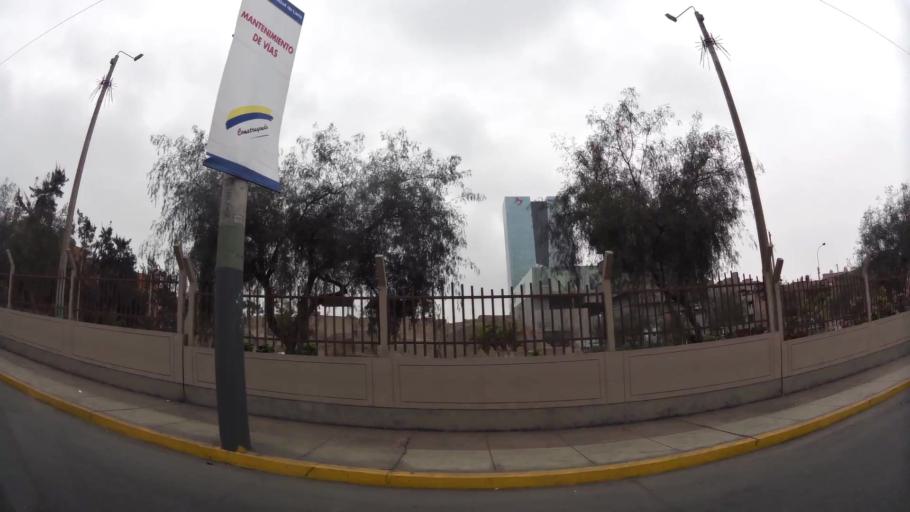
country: PE
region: Lima
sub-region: Lima
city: San Luis
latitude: -12.0837
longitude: -77.0004
